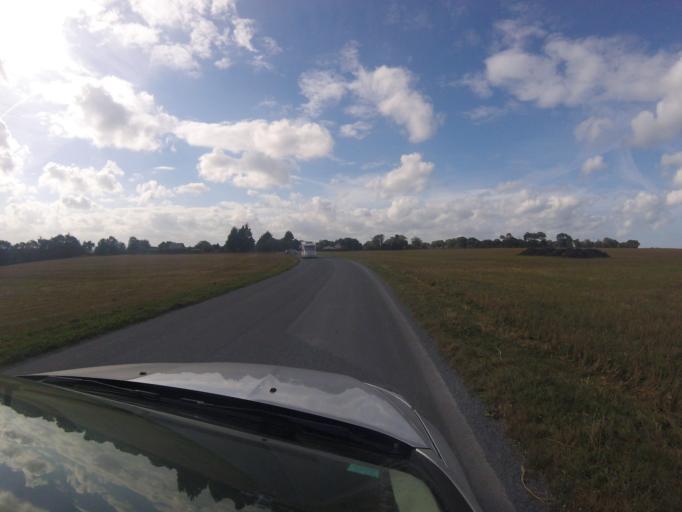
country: FR
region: Lower Normandy
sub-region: Departement du Calvados
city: Saint-Vigor-le-Grand
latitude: 49.3335
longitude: -0.6852
